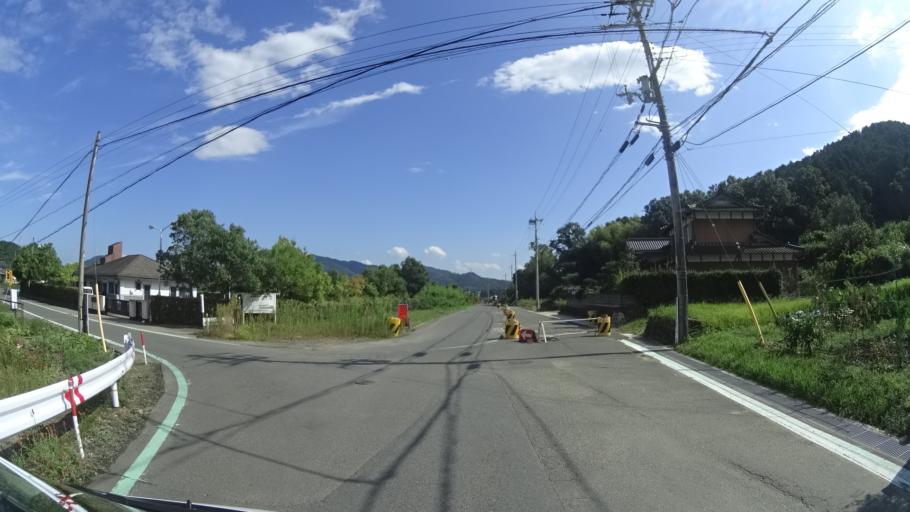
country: JP
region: Kyoto
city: Fukuchiyama
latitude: 35.3188
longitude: 135.1816
